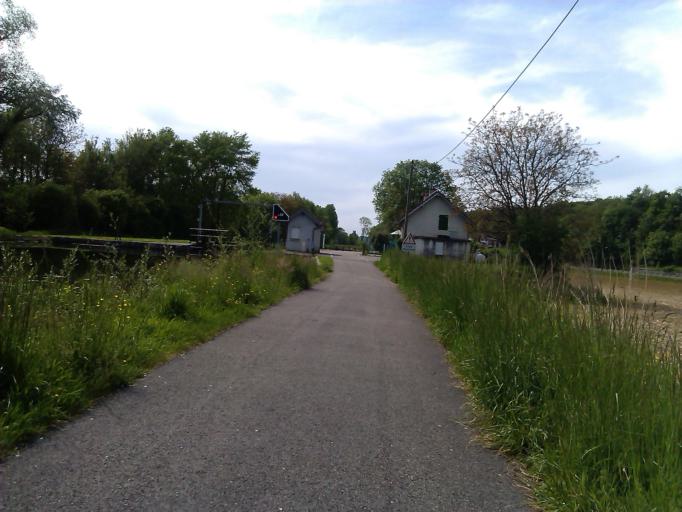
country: FR
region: Franche-Comte
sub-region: Departement du Doubs
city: Saint-Vit
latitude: 47.1663
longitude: 5.8431
